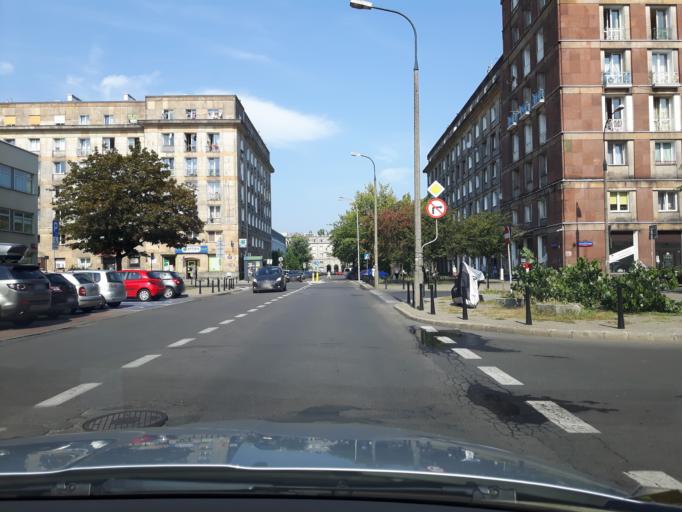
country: PL
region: Masovian Voivodeship
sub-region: Warszawa
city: Praga Polnoc
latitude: 52.2613
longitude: 21.0309
